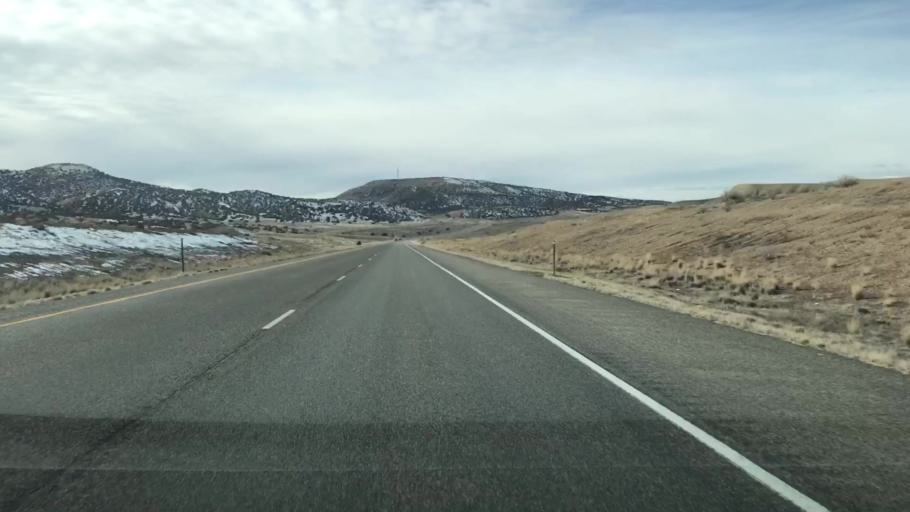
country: US
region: Colorado
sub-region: Mesa County
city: Loma
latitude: 39.2252
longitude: -108.9356
